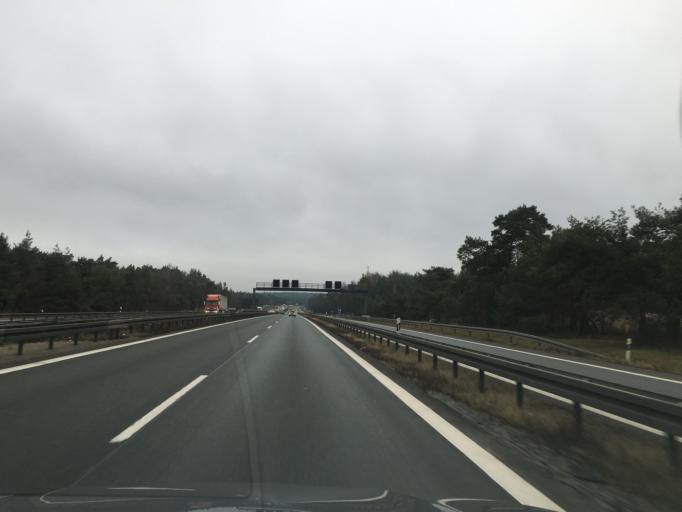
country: DE
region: Bavaria
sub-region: Regierungsbezirk Mittelfranken
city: Rothenbach an der Pegnitz
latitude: 49.4596
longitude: 11.2449
